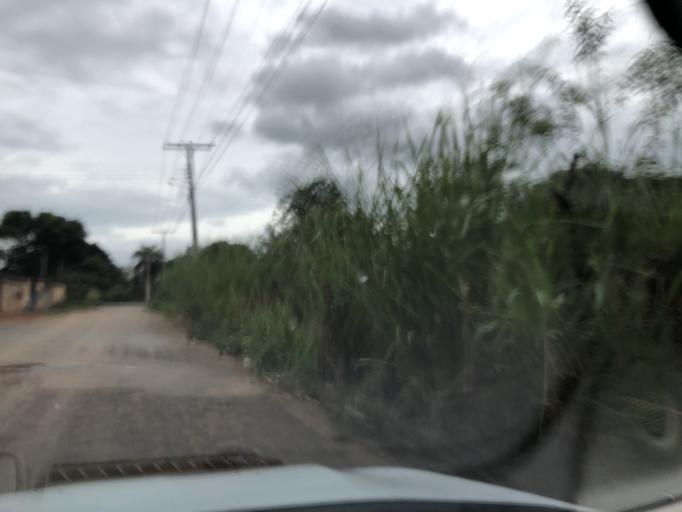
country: BR
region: Goias
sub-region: Luziania
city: Luziania
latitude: -16.1586
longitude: -47.9474
